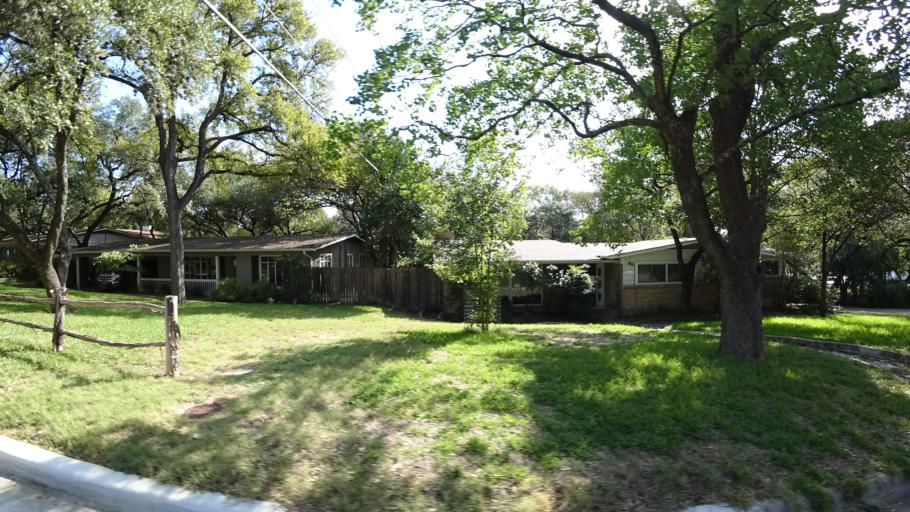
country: US
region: Texas
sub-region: Travis County
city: West Lake Hills
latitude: 30.3382
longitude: -97.7576
